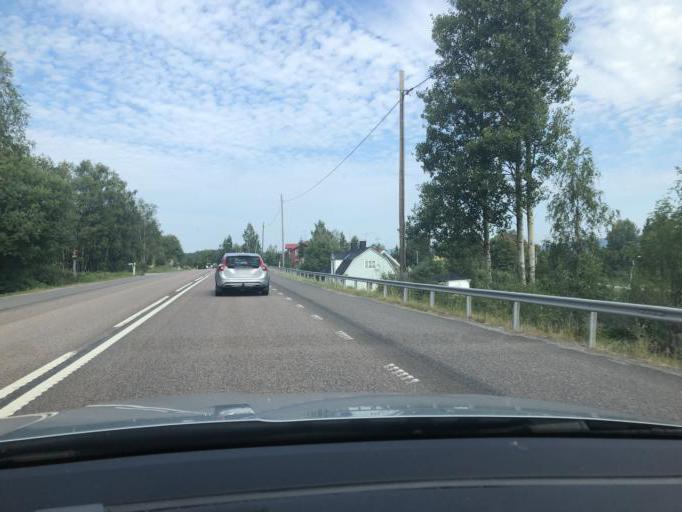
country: SE
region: Vaesternorrland
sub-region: Kramfors Kommun
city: Kramfors
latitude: 62.8877
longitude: 17.8525
